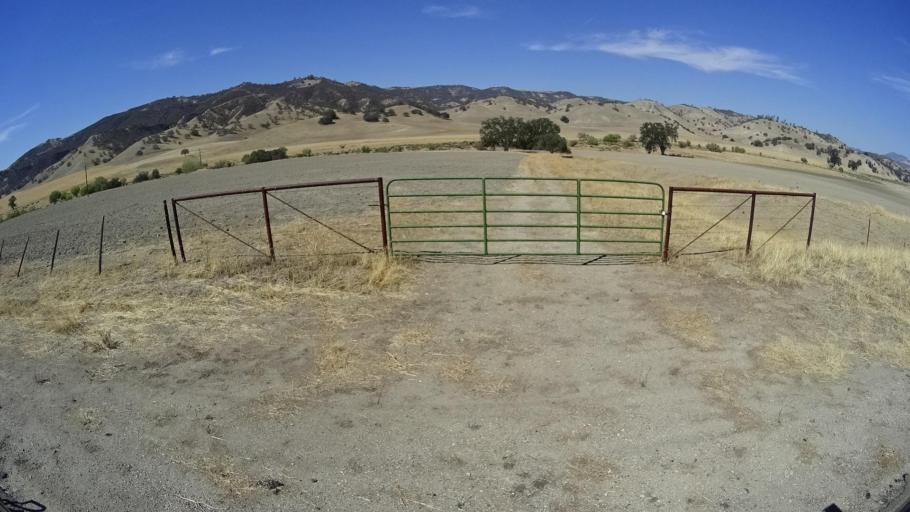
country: US
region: California
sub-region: San Luis Obispo County
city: San Miguel
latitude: 35.9449
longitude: -120.6644
